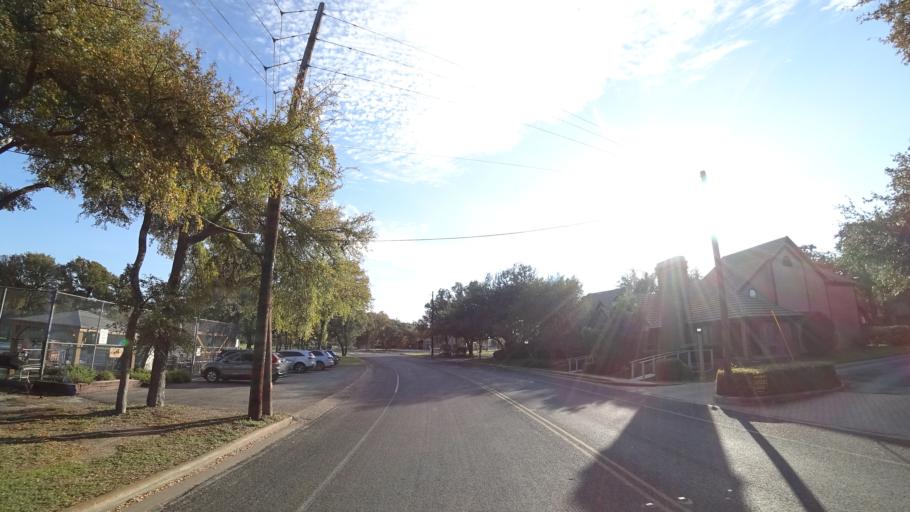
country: US
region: Texas
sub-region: Williamson County
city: Anderson Mill
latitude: 30.4414
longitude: -97.8063
